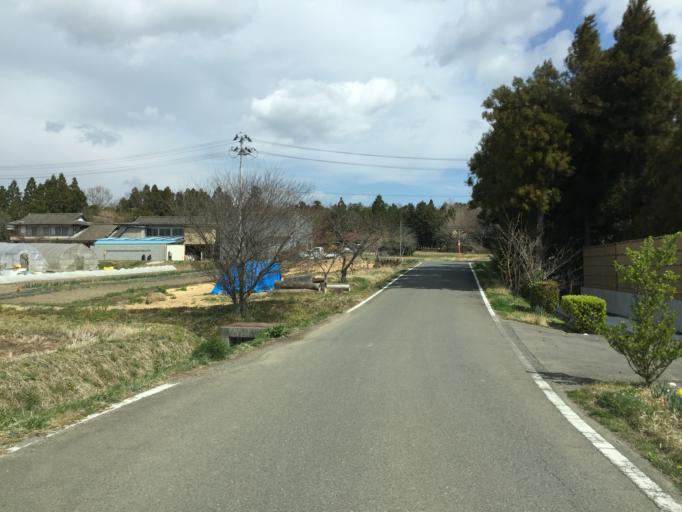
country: JP
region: Miyagi
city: Marumori
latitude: 37.7728
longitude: 140.9243
